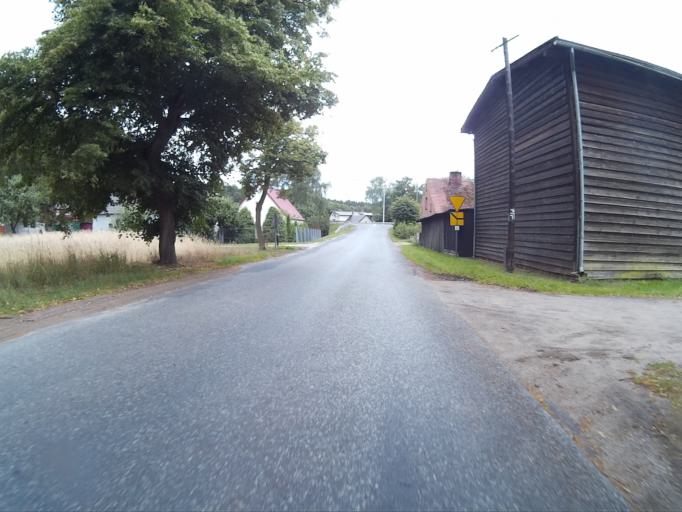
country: PL
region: Kujawsko-Pomorskie
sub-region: Powiat tucholski
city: Tuchola
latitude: 53.5642
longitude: 17.9008
